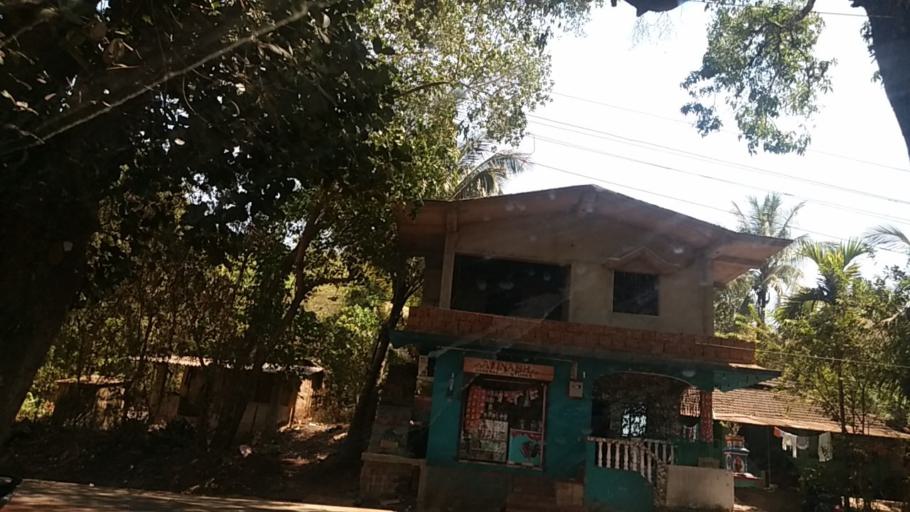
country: IN
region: Goa
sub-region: North Goa
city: Aldona
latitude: 15.5724
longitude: 73.9062
